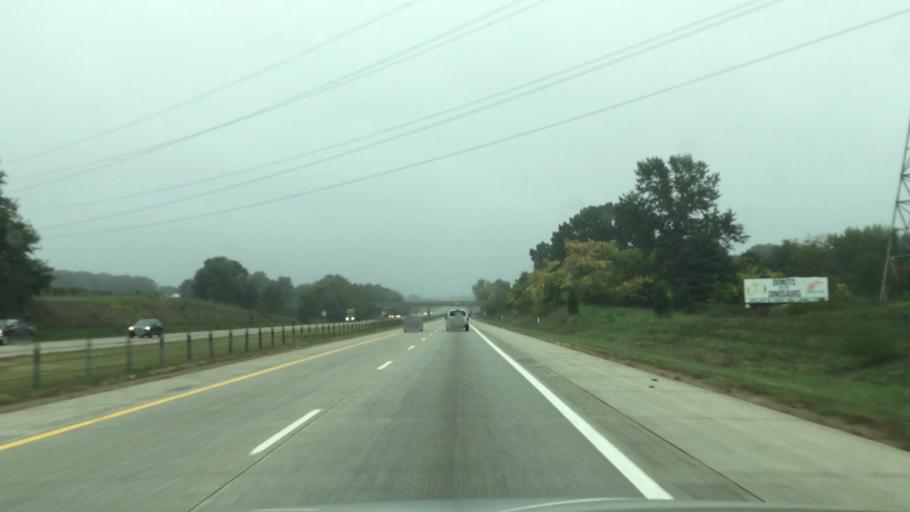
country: US
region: Michigan
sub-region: Berrien County
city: Coloma
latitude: 42.1592
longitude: -86.3336
